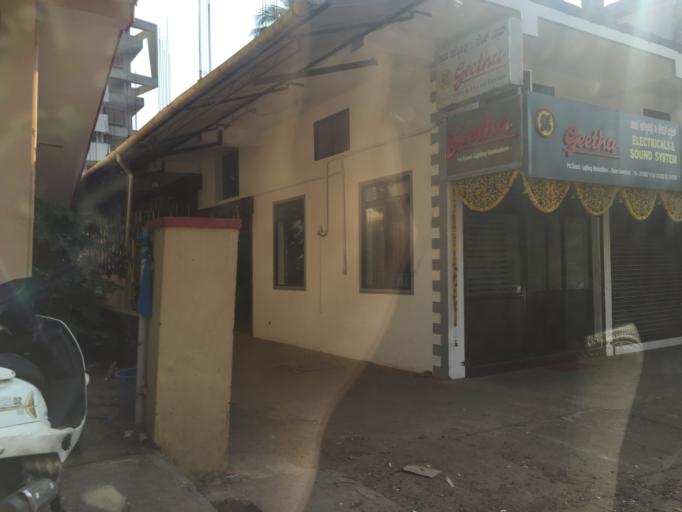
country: IN
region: Karnataka
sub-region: Dakshina Kannada
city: Ullal
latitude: 12.8452
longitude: 74.8448
